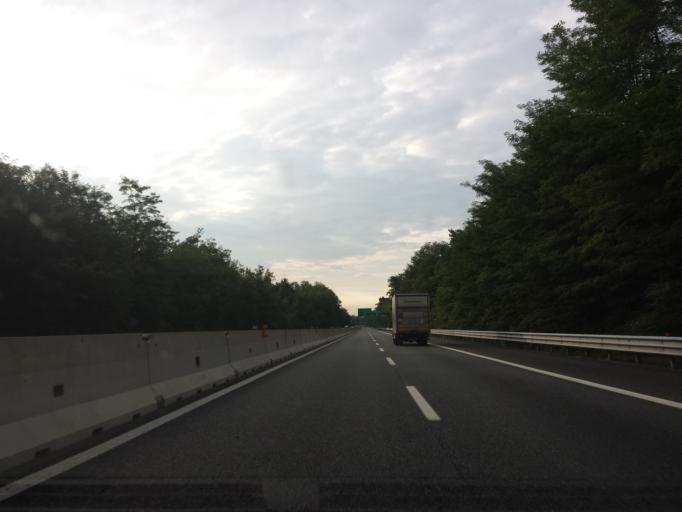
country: IT
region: Lombardy
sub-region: Provincia di Varese
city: Arsago Seprio
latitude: 45.6985
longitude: 8.7457
